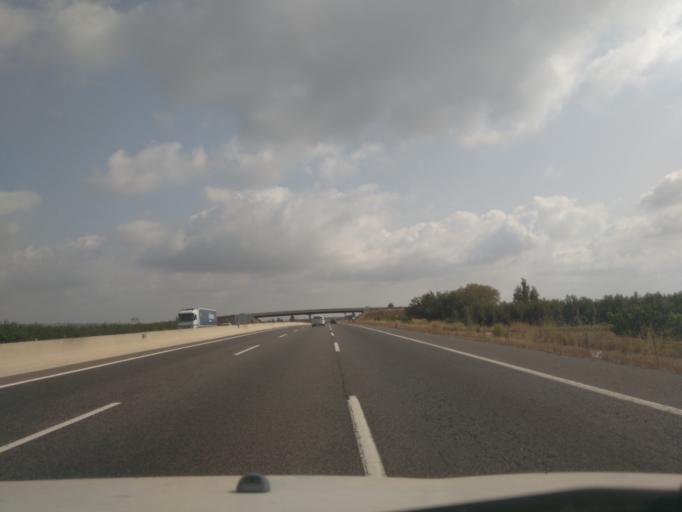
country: ES
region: Valencia
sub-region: Provincia de Valencia
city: L'Alcudia
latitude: 39.2203
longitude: -0.4925
